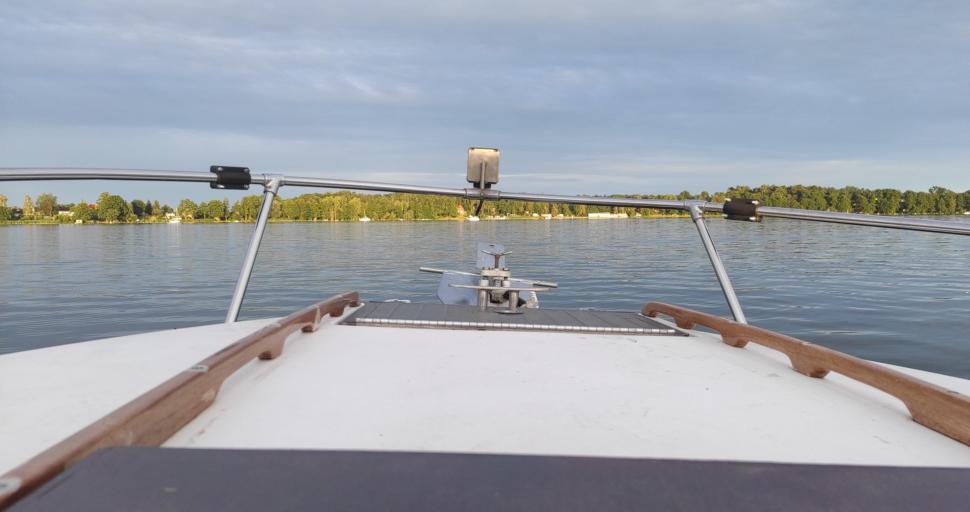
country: DE
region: Brandenburg
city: Friedland
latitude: 52.0217
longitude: 14.1827
